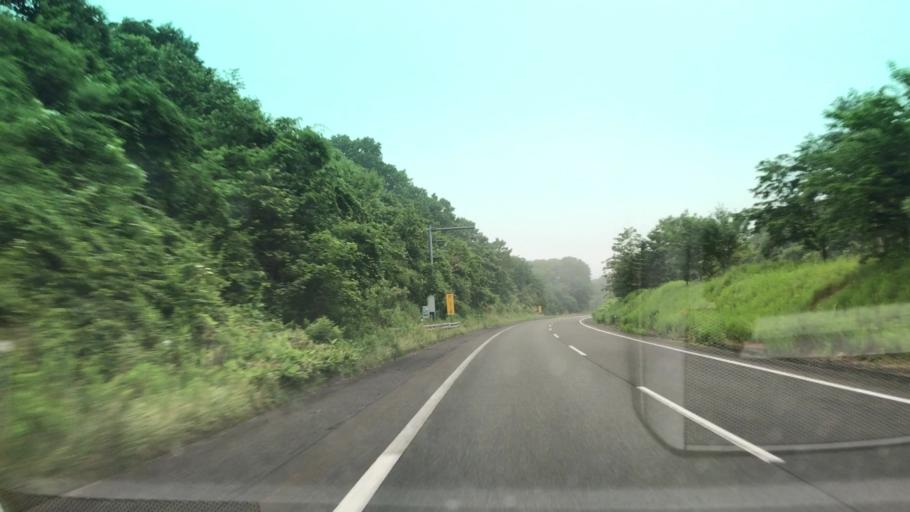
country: JP
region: Hokkaido
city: Shiraoi
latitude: 42.4712
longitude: 141.2114
